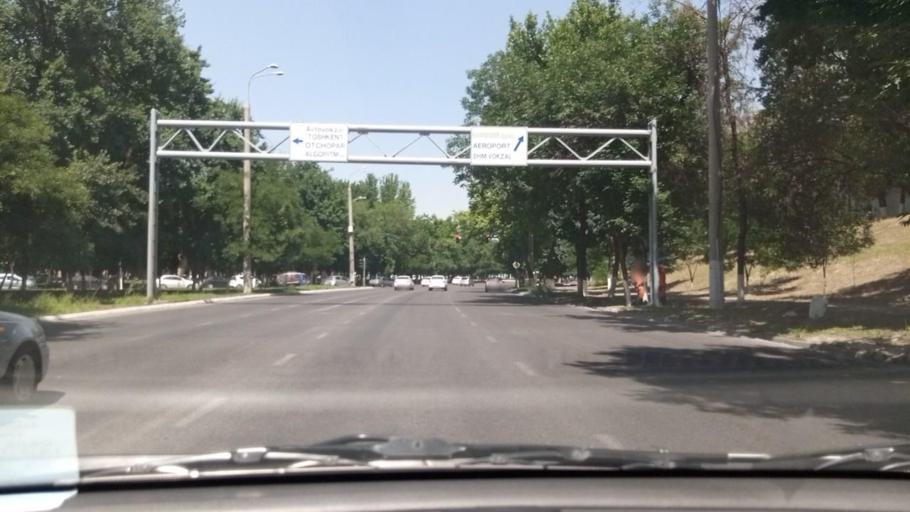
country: UZ
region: Toshkent Shahri
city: Tashkent
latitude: 41.2572
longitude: 69.2168
